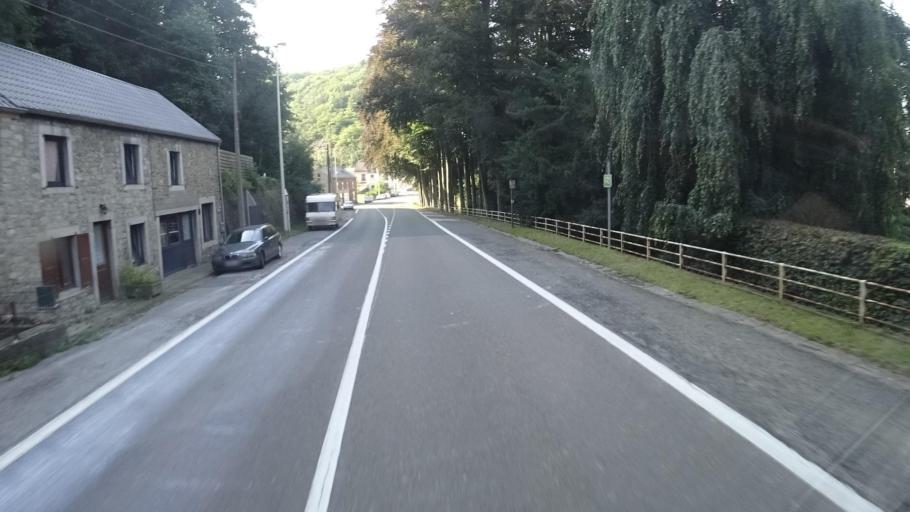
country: BE
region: Wallonia
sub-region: Province de Namur
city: Profondeville
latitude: 50.3595
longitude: 4.8713
